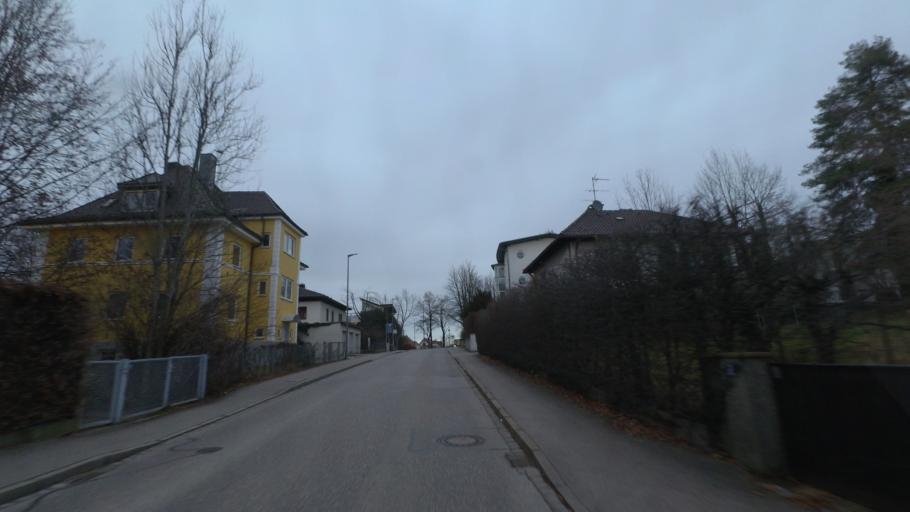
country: DE
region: Bavaria
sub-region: Upper Bavaria
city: Traunstein
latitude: 47.8725
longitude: 12.6339
